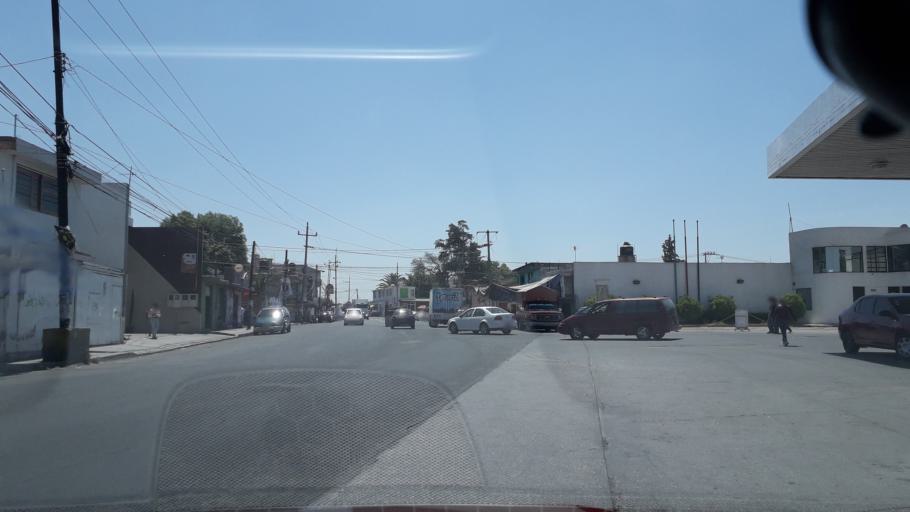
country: MX
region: Puebla
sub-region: Cuautlancingo
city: Sanctorum
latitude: 19.1006
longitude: -98.2285
